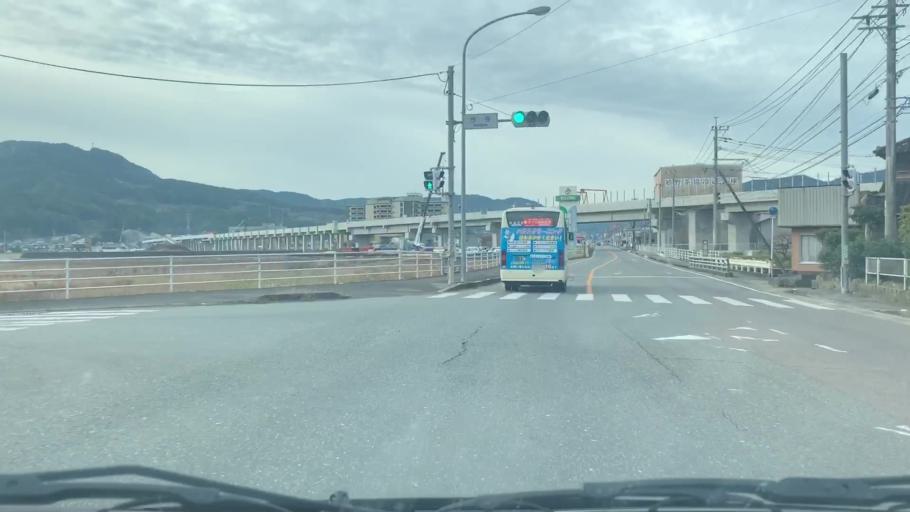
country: JP
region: Saga Prefecture
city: Ureshinomachi-shimojuku
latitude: 33.1101
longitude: 130.0003
